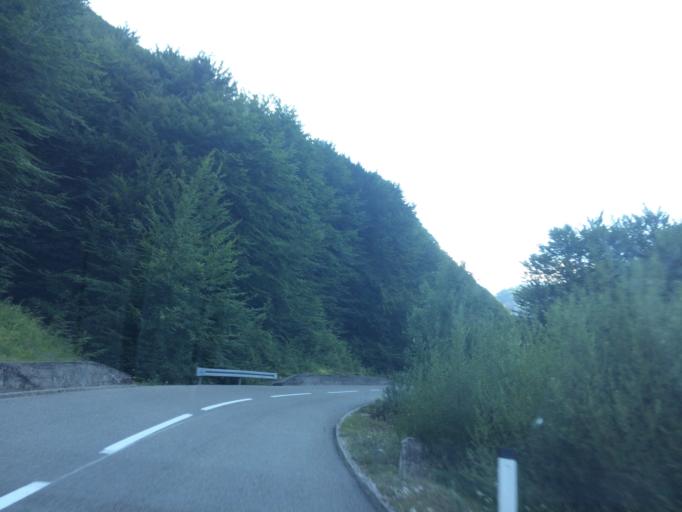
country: ME
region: Opstina Savnik
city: Savnik
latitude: 42.9517
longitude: 19.0975
